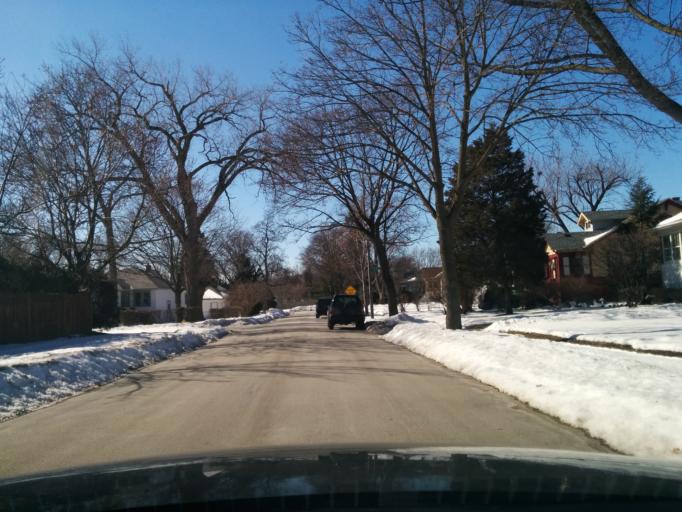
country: US
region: Illinois
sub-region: DuPage County
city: Villa Park
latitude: 41.8969
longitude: -87.9673
